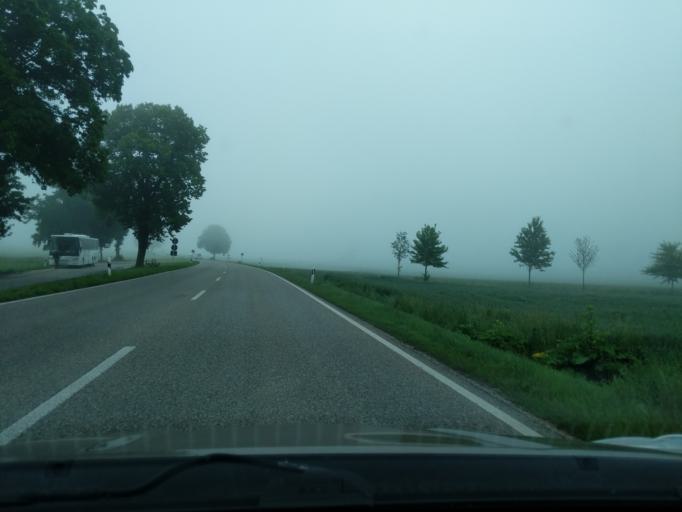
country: DE
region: Bavaria
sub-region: Swabia
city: Gessertshausen
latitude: 48.3375
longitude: 10.7512
